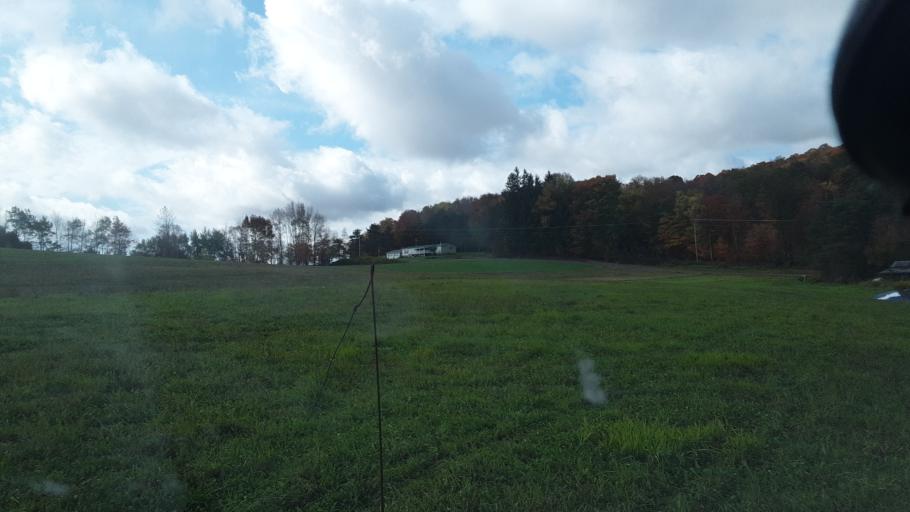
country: US
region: New York
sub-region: Allegany County
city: Andover
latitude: 41.9804
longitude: -77.7602
